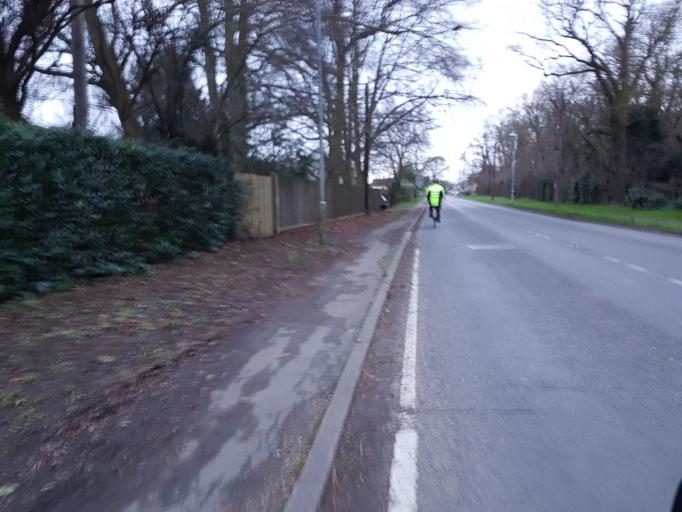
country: GB
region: England
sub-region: Cambridgeshire
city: Bottisham
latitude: 52.2204
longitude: 0.2224
